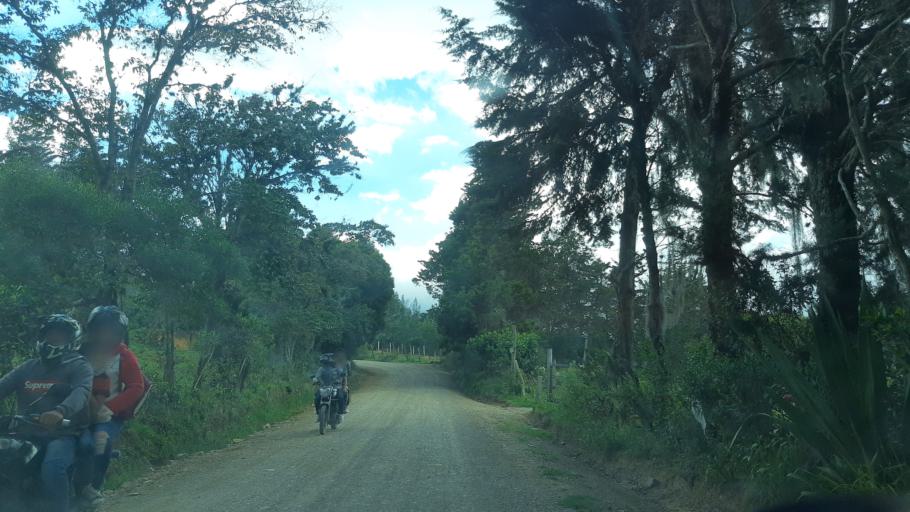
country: CO
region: Boyaca
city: Santa Sofia
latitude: 5.7312
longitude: -73.5962
